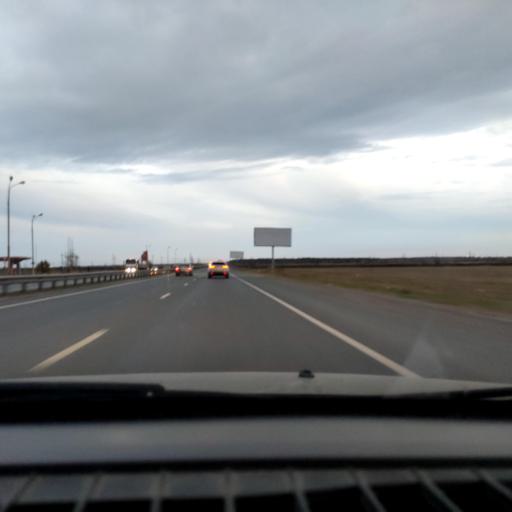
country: RU
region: Samara
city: Zhigulevsk
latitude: 53.5559
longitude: 49.5026
